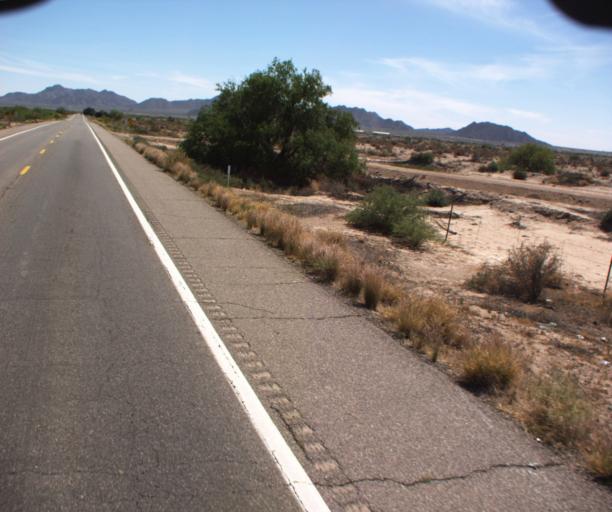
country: US
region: Arizona
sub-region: Pinal County
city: Sacaton
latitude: 33.0962
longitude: -111.7104
